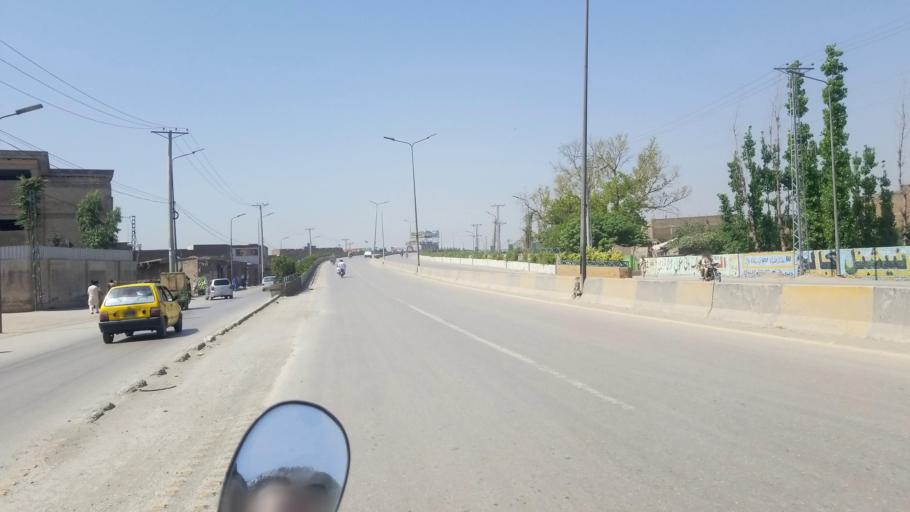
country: PK
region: Khyber Pakhtunkhwa
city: Peshawar
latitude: 33.9808
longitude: 71.5663
